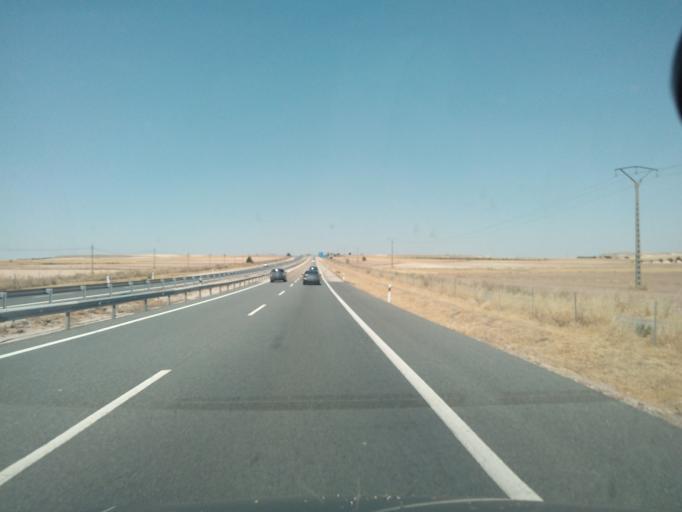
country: ES
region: Castille-La Mancha
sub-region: Province of Toledo
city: Tembleque
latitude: 39.7474
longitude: -3.4859
